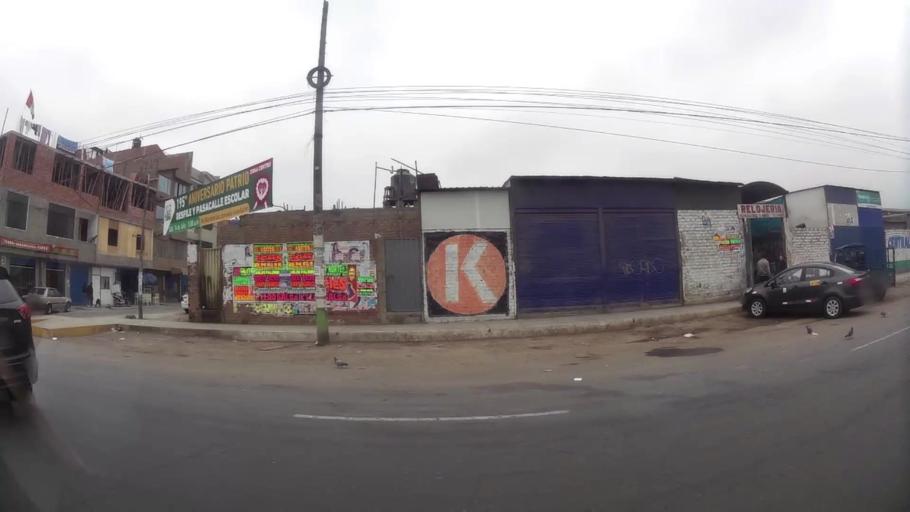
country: PE
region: Lima
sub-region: Lima
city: Independencia
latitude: -11.9699
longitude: -77.0792
